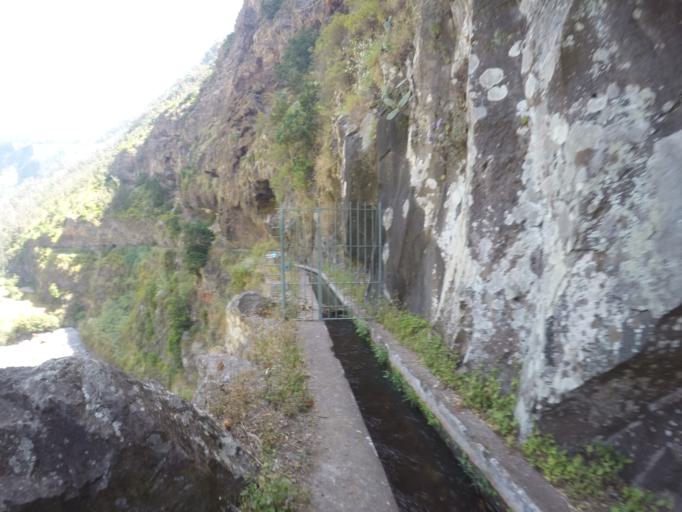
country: PT
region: Madeira
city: Camara de Lobos
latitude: 32.6684
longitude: -16.9585
